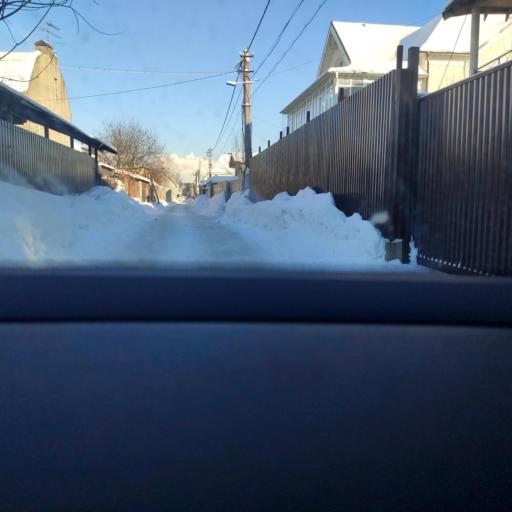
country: RU
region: Moskovskaya
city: Mosrentgen
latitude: 55.6258
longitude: 37.4623
